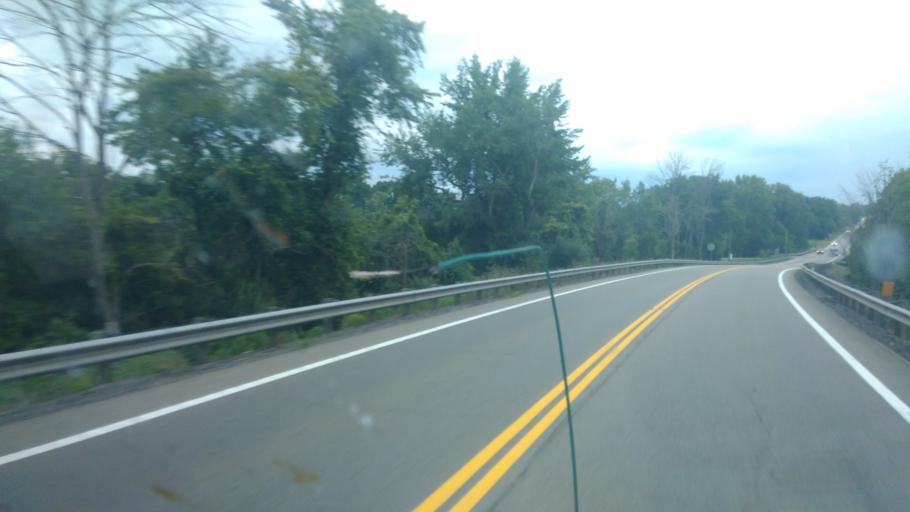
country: US
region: Ohio
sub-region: Licking County
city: Granville South
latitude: 40.0185
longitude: -82.5244
